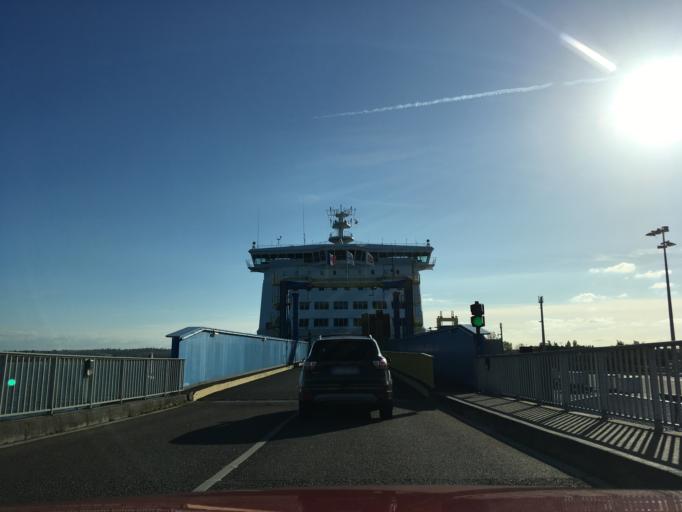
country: FR
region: Lower Normandy
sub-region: Departement du Calvados
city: Ouistreham
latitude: 49.2901
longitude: -0.2477
